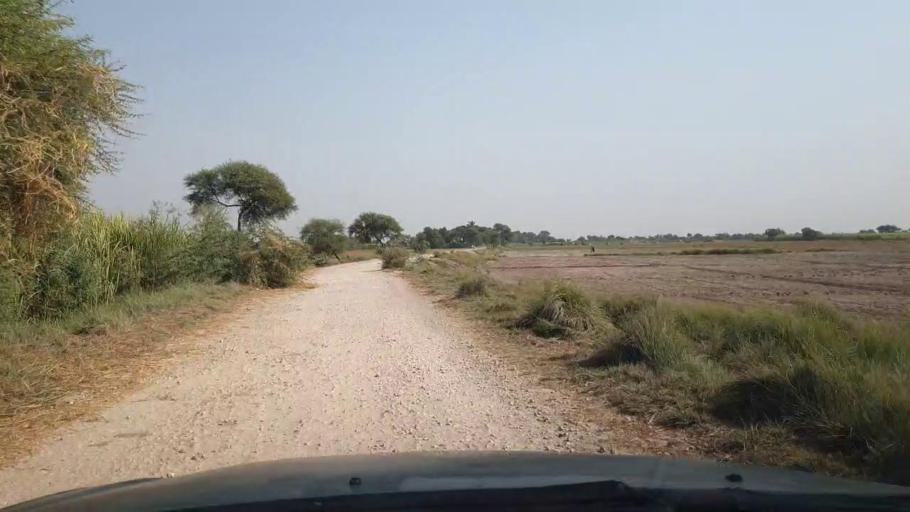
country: PK
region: Sindh
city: Bulri
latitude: 24.9111
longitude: 68.3684
